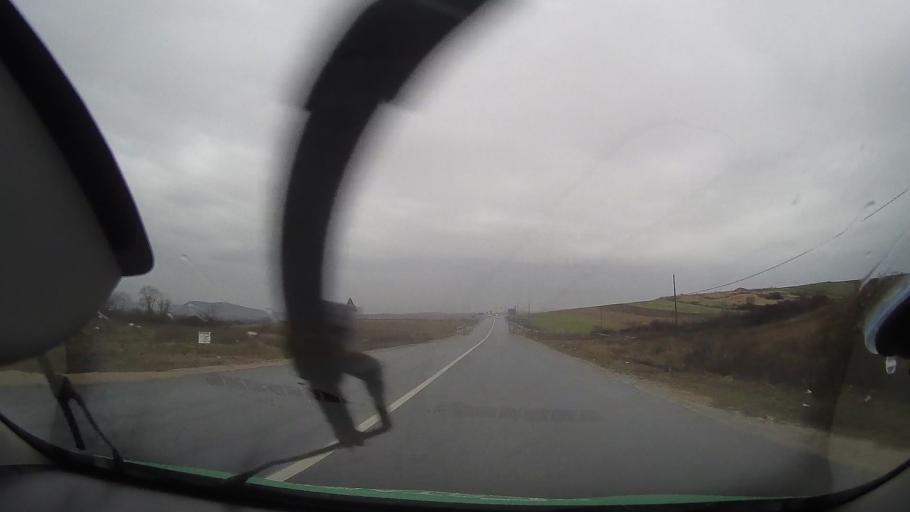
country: RO
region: Bihor
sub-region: Comuna Pocola
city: Pocola
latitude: 46.6808
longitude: 22.3118
